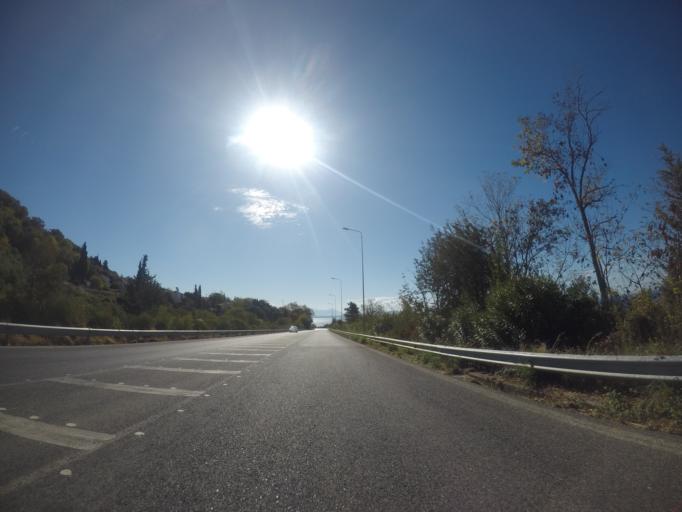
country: GR
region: Epirus
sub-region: Nomos Prevezis
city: Neos Oropos
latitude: 39.1066
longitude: 20.6361
